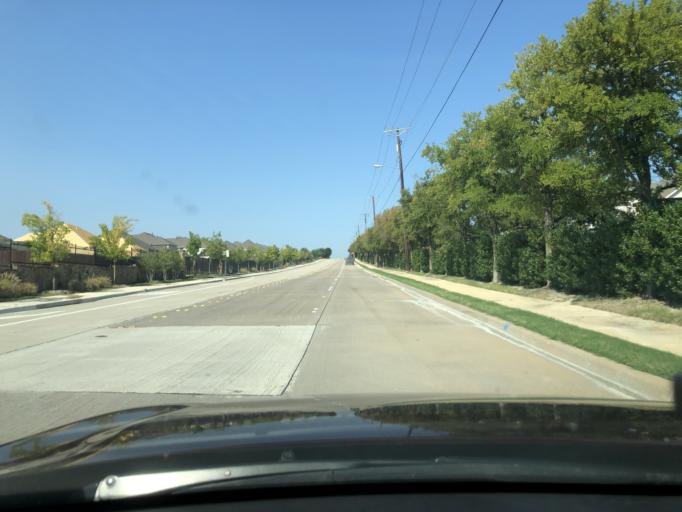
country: US
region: Texas
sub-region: Rockwall County
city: Rockwall
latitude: 32.9411
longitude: -96.4635
